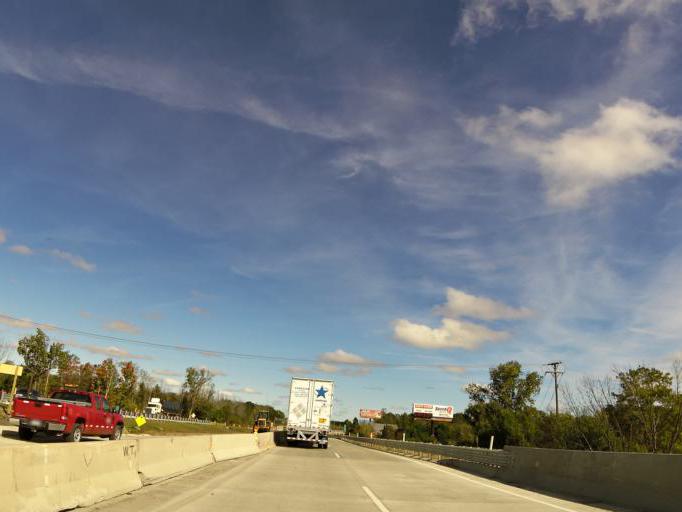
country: US
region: Michigan
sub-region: Saint Clair County
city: Port Huron
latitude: 42.9797
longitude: -82.4753
